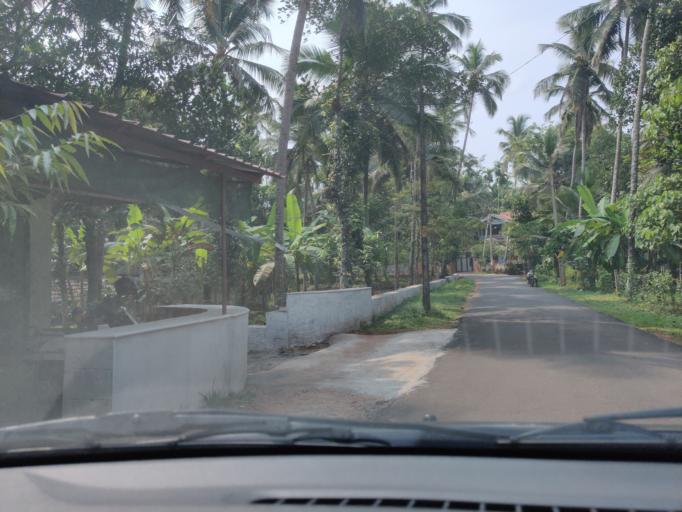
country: IN
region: Kerala
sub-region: Kozhikode
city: Kunnamangalam
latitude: 11.4188
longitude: 75.8734
